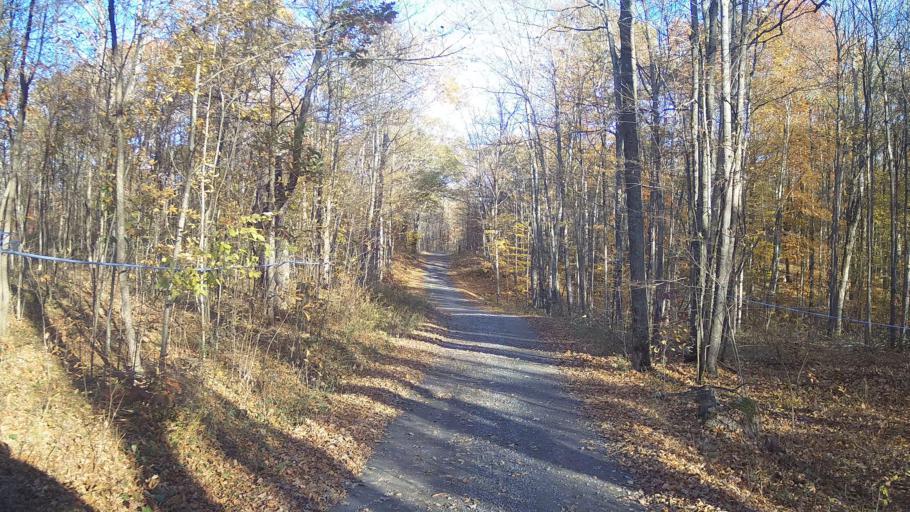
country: CA
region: Ontario
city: Perth
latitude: 44.7352
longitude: -76.4258
